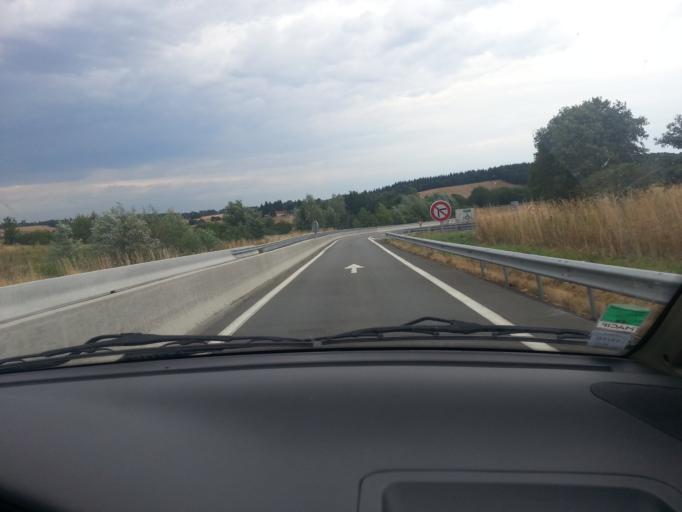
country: FR
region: Auvergne
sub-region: Departement de l'Allier
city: Lapalisse
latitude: 46.2195
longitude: 3.6778
